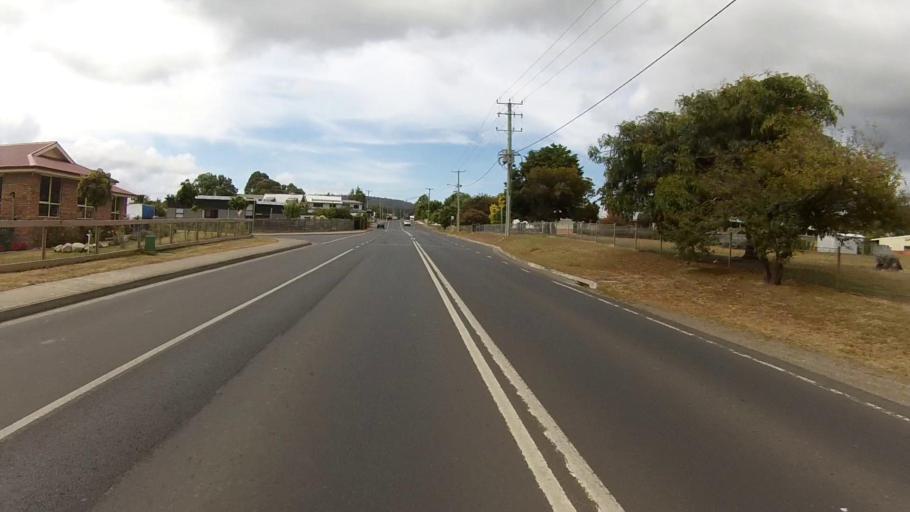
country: AU
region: Tasmania
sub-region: Kingborough
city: Margate
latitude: -43.0644
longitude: 147.2541
